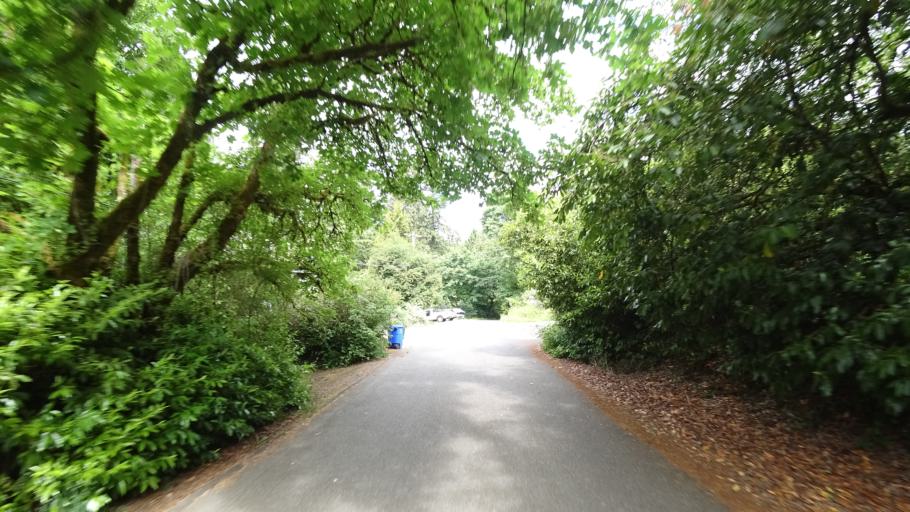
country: US
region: Oregon
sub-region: Clackamas County
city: Lake Oswego
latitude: 45.4529
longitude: -122.6893
